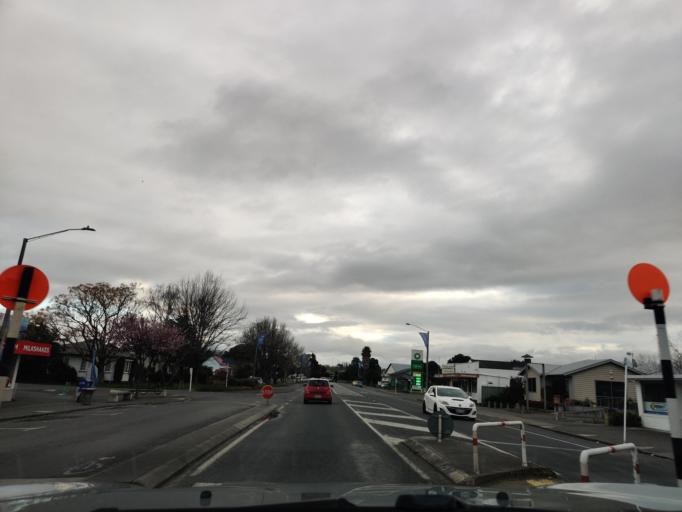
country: NZ
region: Hawke's Bay
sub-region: Napier City
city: Taradale
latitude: -39.5837
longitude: 176.9158
